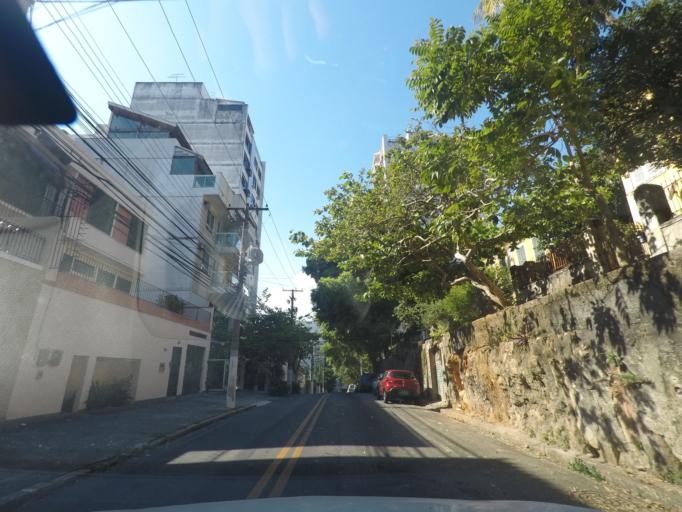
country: BR
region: Rio de Janeiro
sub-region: Niteroi
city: Niteroi
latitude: -22.9073
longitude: -43.1299
